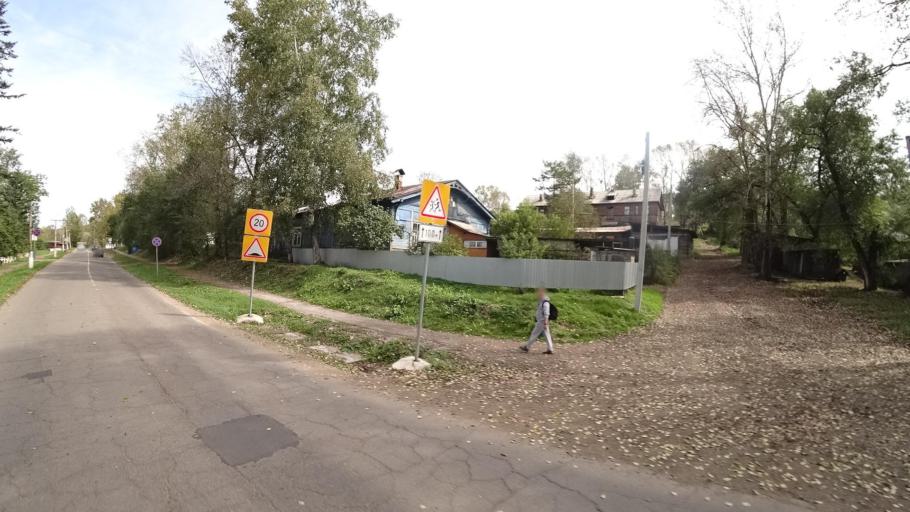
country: RU
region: Jewish Autonomous Oblast
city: Khingansk
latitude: 49.0150
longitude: 131.0595
